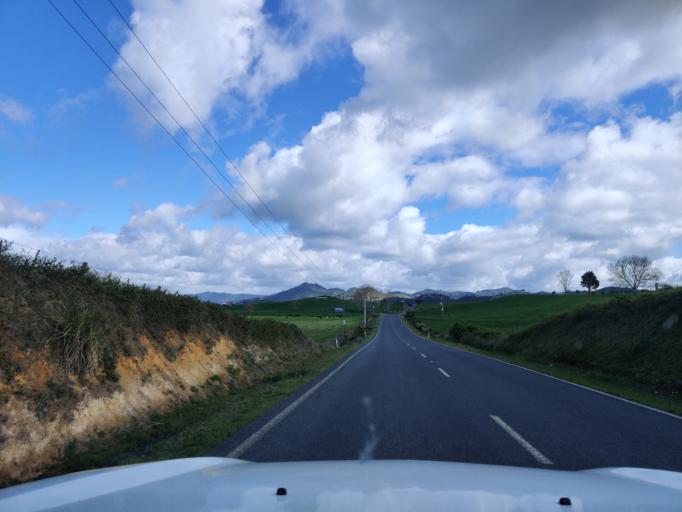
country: NZ
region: Waikato
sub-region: Waikato District
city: Ngaruawahia
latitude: -37.5744
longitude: 175.2420
